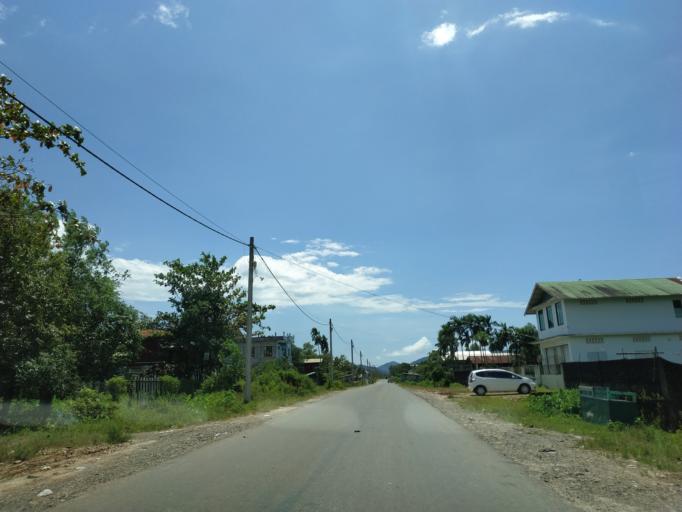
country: MM
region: Tanintharyi
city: Dawei
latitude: 14.0990
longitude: 98.1909
